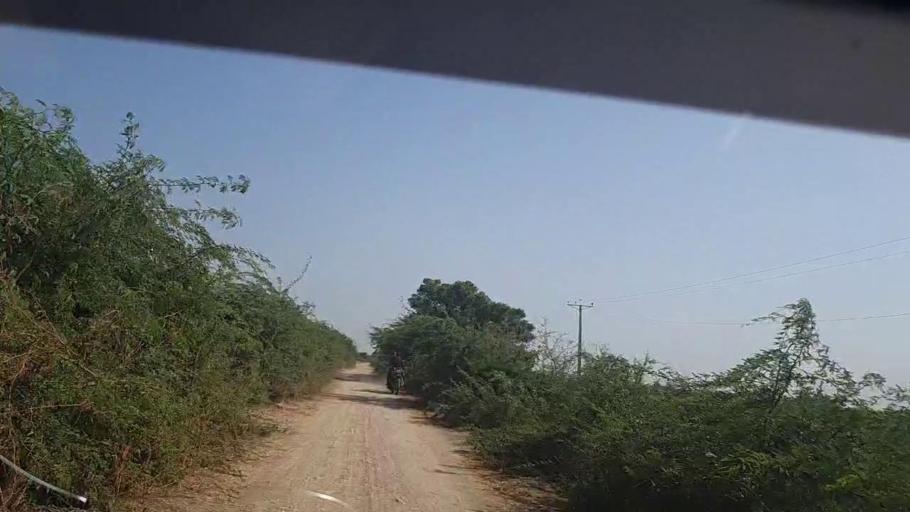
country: PK
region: Sindh
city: Rajo Khanani
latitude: 24.9602
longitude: 68.8928
